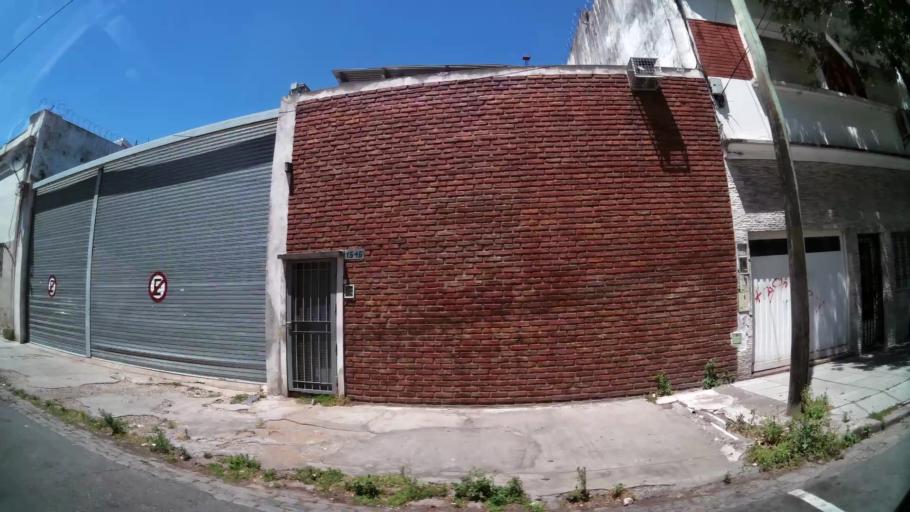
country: AR
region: Buenos Aires F.D.
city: Buenos Aires
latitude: -34.6324
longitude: -58.3872
